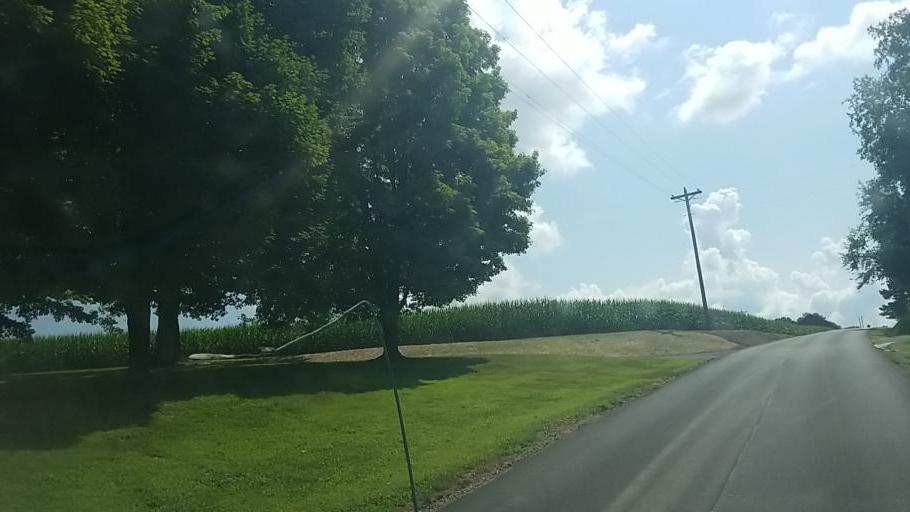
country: US
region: Ohio
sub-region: Richland County
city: Lincoln Heights
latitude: 40.6887
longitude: -82.3885
